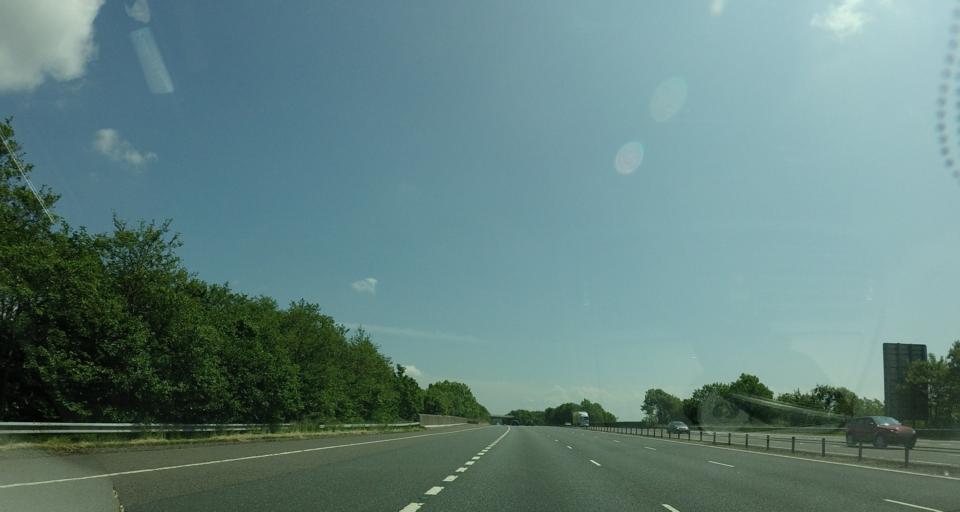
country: GB
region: Scotland
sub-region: Dumfries and Galloway
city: Annan
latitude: 55.0498
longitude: -3.2127
